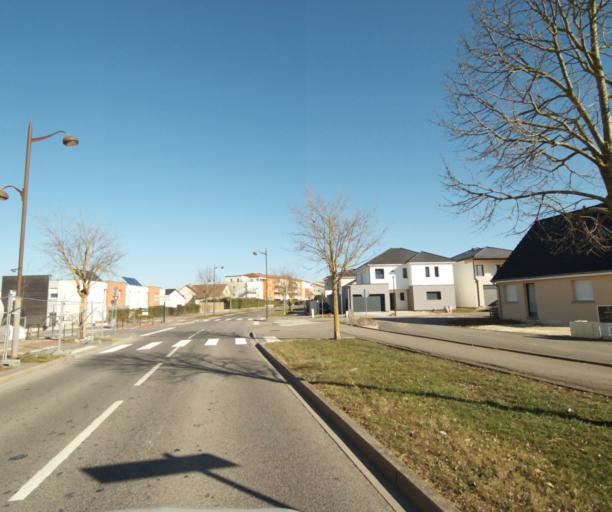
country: FR
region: Lorraine
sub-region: Departement de Meurthe-et-Moselle
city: Pulnoy
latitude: 48.6995
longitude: 6.2506
